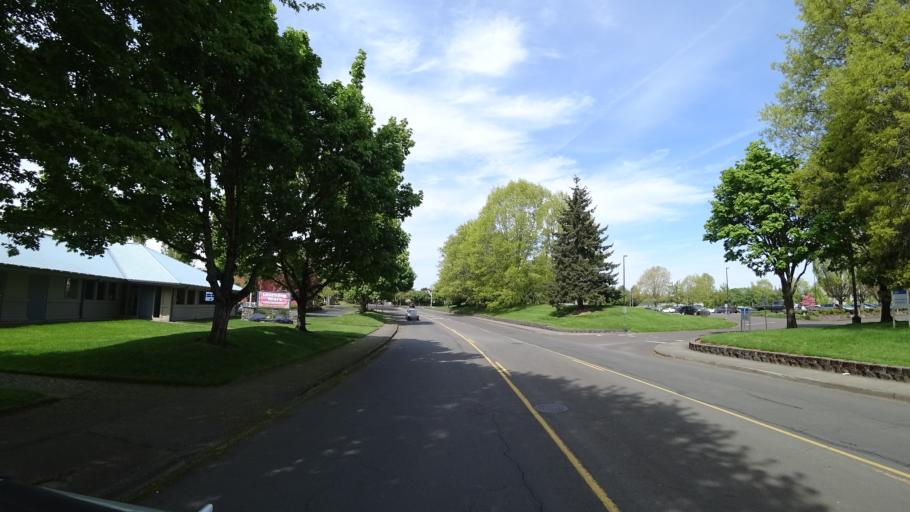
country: US
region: Oregon
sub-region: Washington County
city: Rockcreek
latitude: 45.5322
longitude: -122.9314
